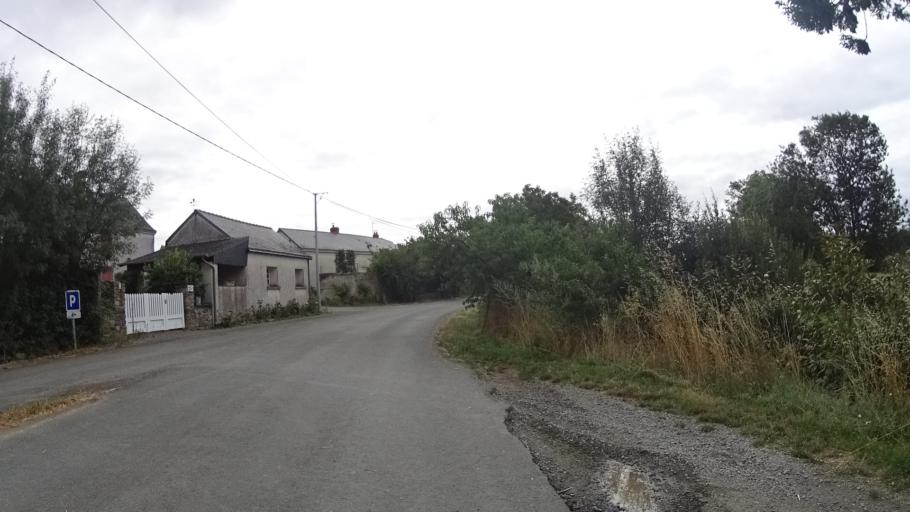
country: FR
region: Pays de la Loire
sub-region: Departement de Maine-et-Loire
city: Saint-Germain-des-Pres
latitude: 47.3740
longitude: -0.8122
